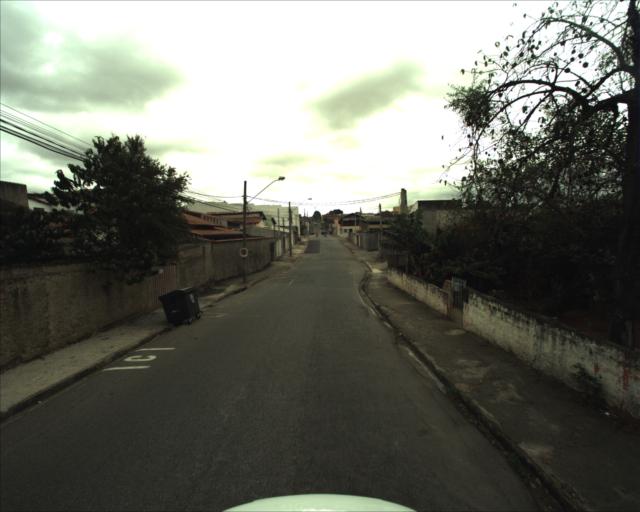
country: BR
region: Sao Paulo
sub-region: Sorocaba
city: Sorocaba
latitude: -23.4786
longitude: -47.4676
